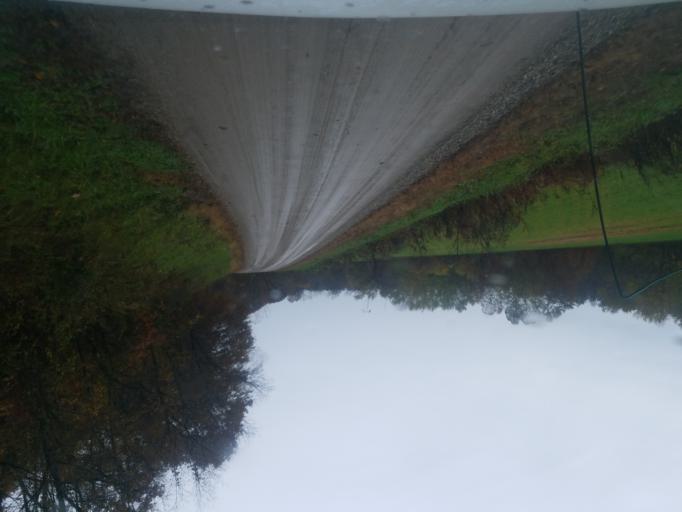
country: US
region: Ohio
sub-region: Washington County
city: Beverly
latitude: 39.4577
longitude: -81.7724
